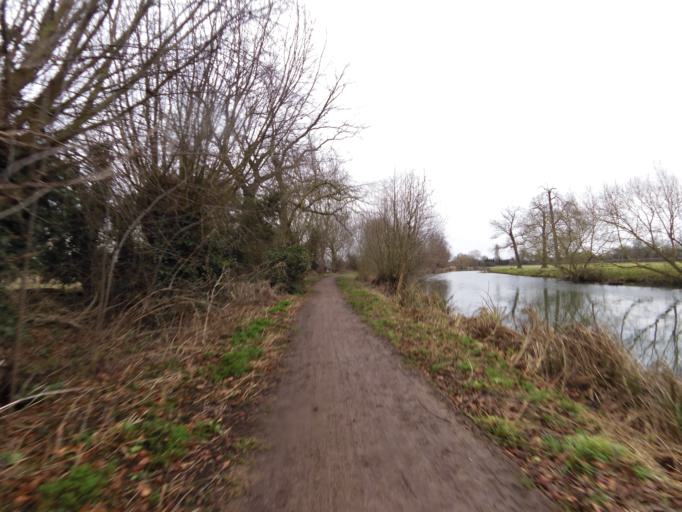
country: GB
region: England
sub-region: Cambridgeshire
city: Waterbeach
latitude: 52.2547
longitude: 0.1917
